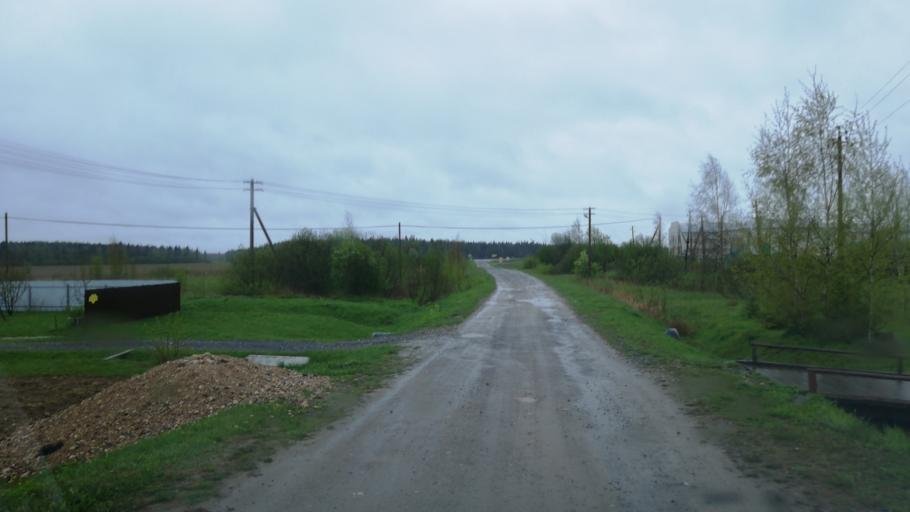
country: RU
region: Jaroslavl
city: Danilov
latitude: 57.9937
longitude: 40.1817
